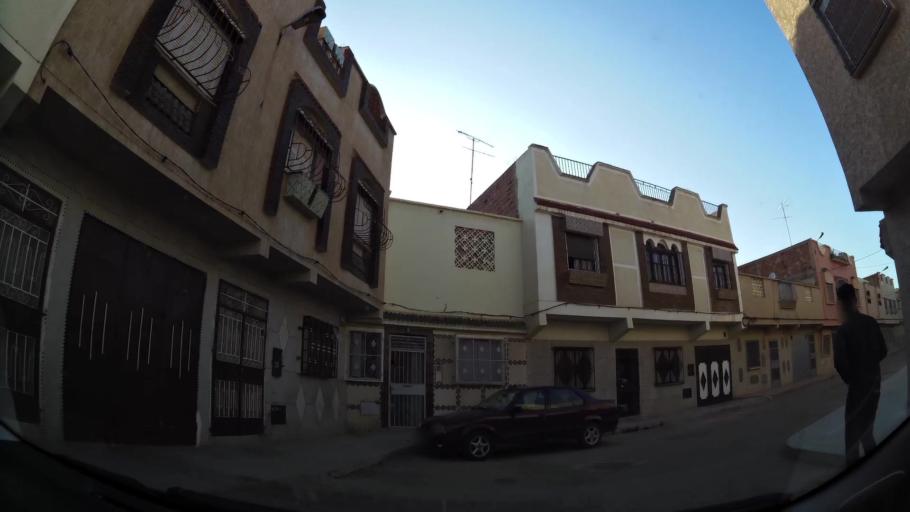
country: MA
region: Oriental
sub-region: Oujda-Angad
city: Oujda
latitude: 34.7036
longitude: -1.8977
